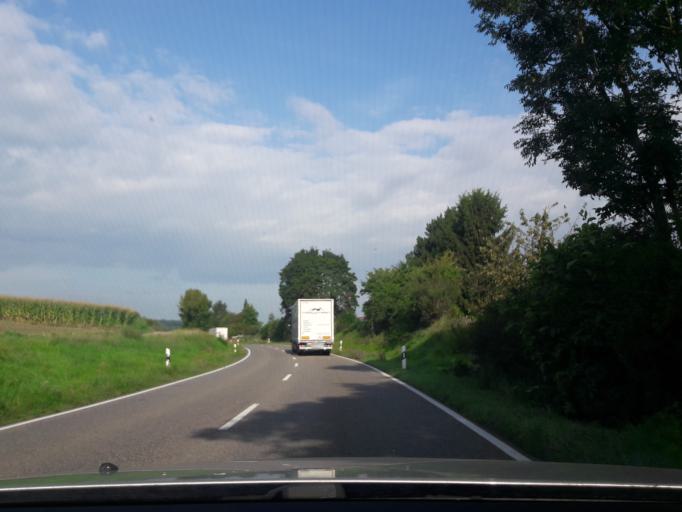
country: DE
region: Baden-Wuerttemberg
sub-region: Regierungsbezirk Stuttgart
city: Grossbottwar
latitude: 48.9943
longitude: 9.2992
